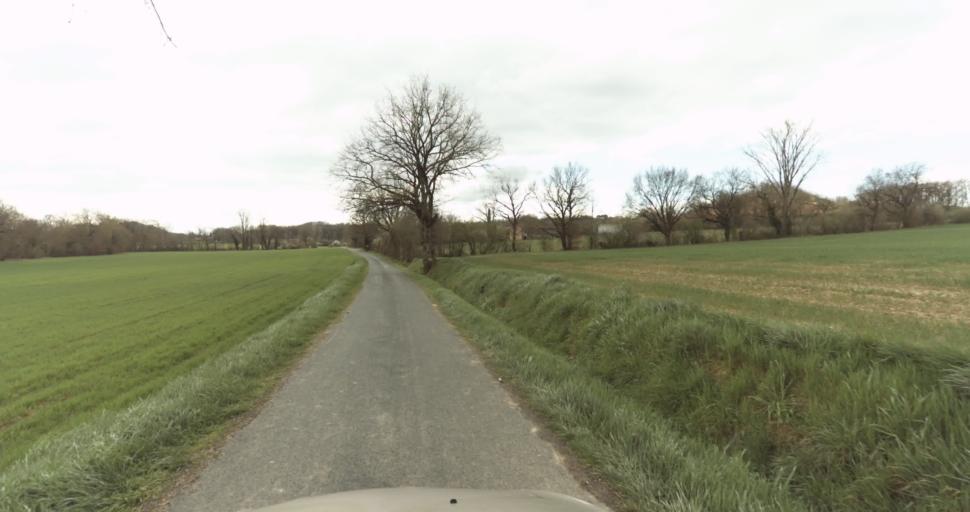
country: FR
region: Midi-Pyrenees
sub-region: Departement du Tarn
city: Puygouzon
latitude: 43.8834
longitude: 2.1955
